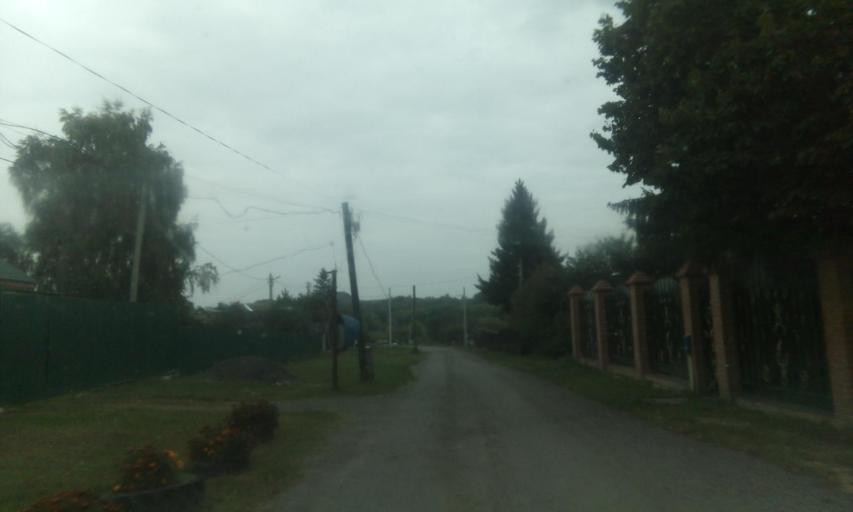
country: RU
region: Tula
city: Dubovka
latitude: 53.9462
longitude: 38.0225
